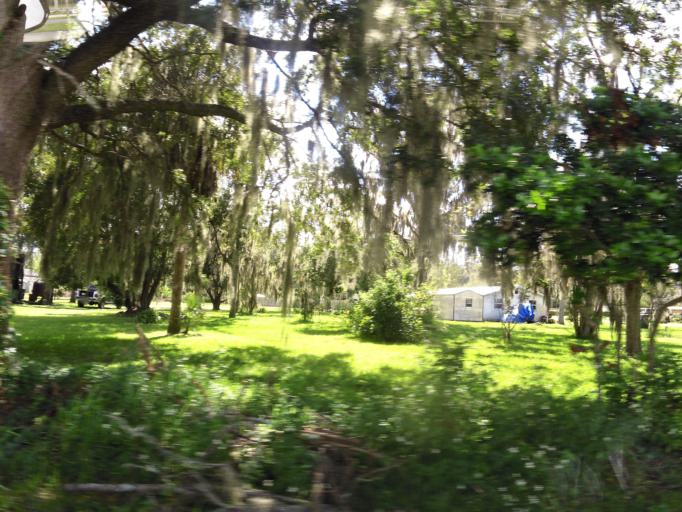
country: US
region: Florida
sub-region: Union County
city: Lake Butler
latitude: 30.0221
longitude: -82.3427
